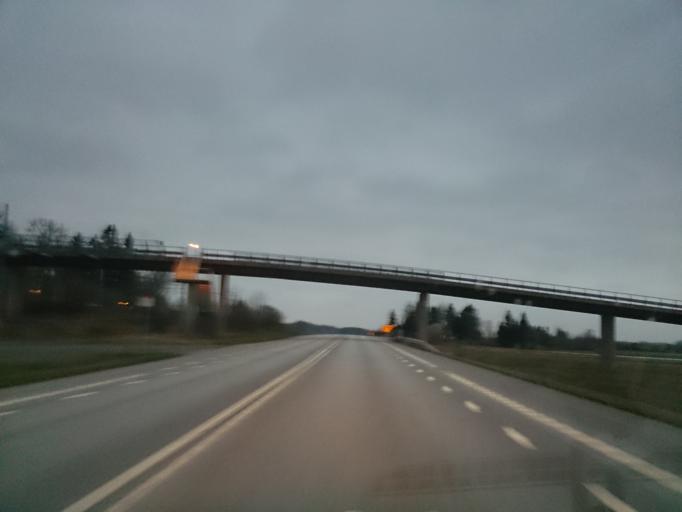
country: SE
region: OEstergoetland
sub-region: Linkopings Kommun
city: Linghem
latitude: 58.4495
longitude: 15.8268
